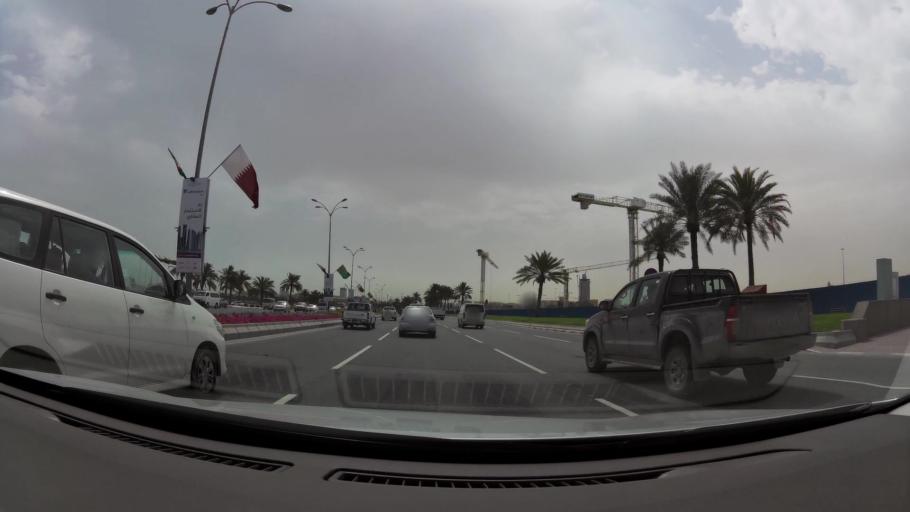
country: QA
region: Baladiyat ad Dawhah
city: Doha
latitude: 25.3012
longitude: 51.5183
